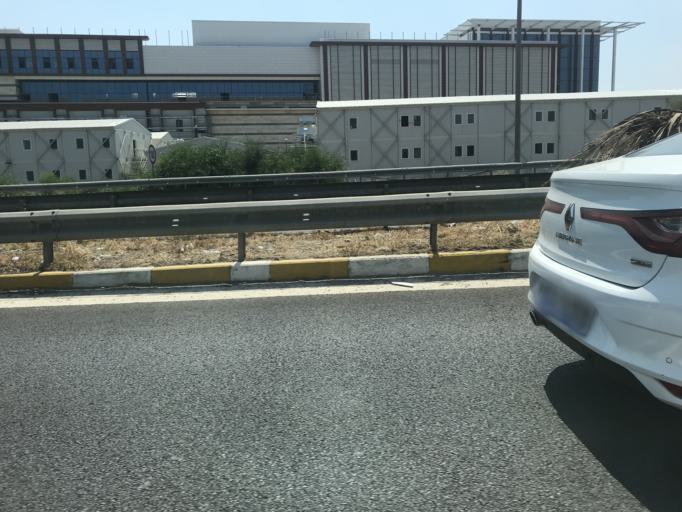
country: TR
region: Izmir
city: Karsiyaka
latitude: 38.4002
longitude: 27.0663
